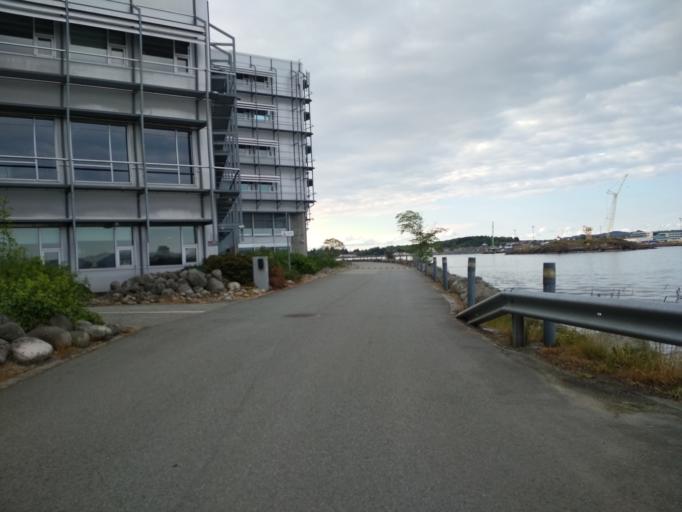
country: NO
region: Rogaland
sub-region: Stavanger
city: Stavanger
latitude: 58.9783
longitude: 5.7209
